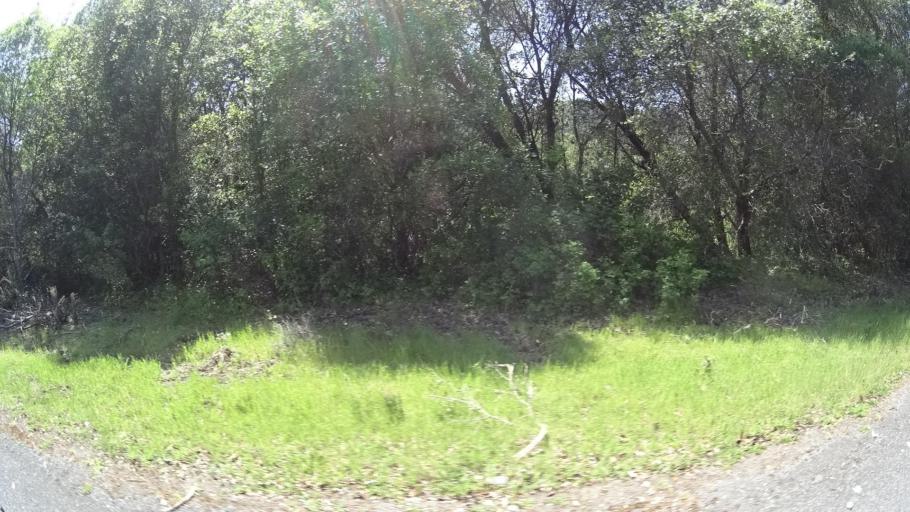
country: US
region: California
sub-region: Humboldt County
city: Redway
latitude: 40.2235
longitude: -123.6381
